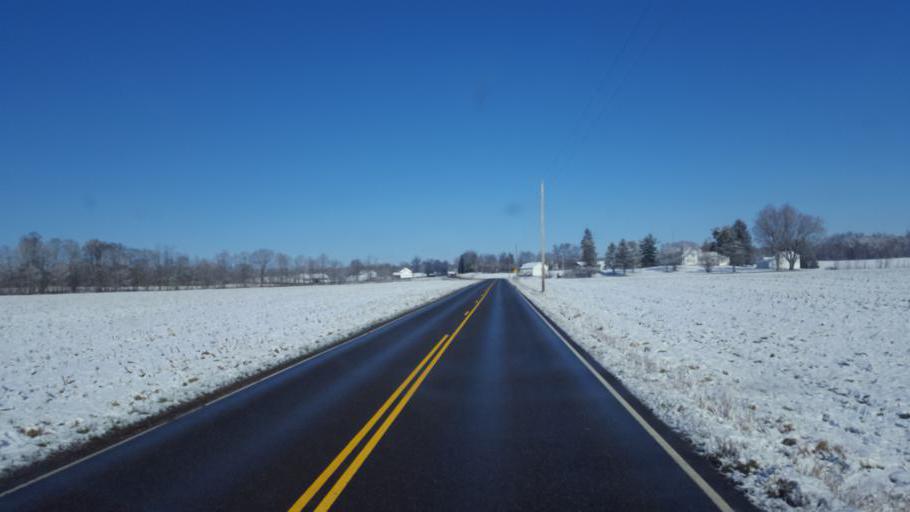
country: US
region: Ohio
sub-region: Knox County
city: Fredericktown
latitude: 40.5378
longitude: -82.6098
